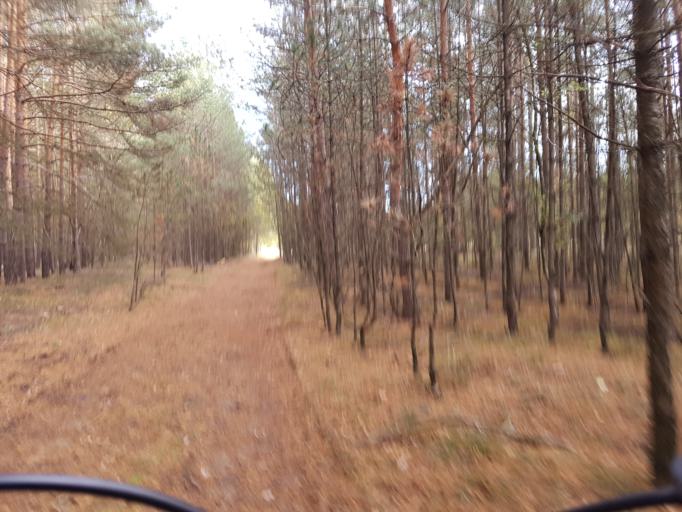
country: DE
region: Brandenburg
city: Schilda
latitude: 51.5870
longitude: 13.3516
